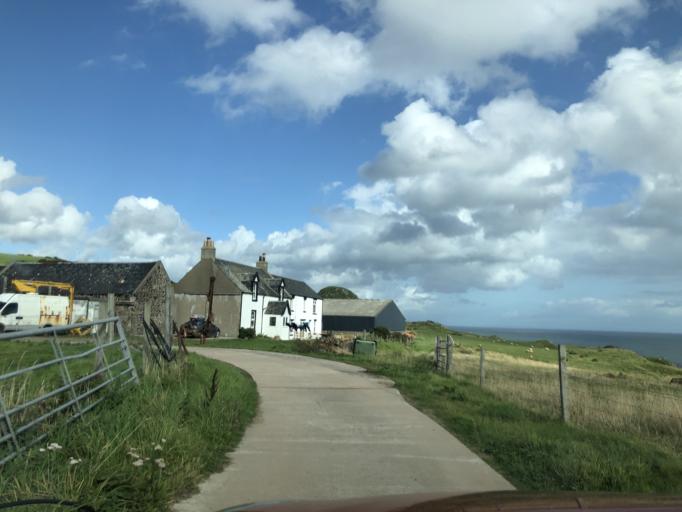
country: GB
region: Scotland
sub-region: Argyll and Bute
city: Campbeltown
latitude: 55.3103
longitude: -5.6067
